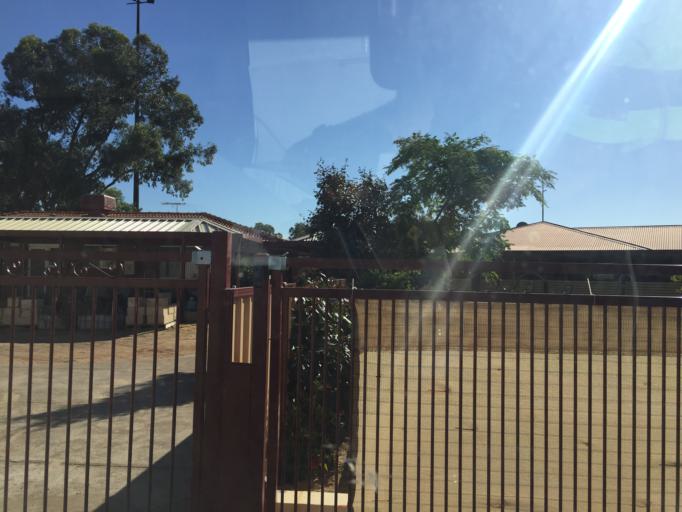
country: AU
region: Western Australia
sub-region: Mundaring
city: Swan View
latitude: -31.8840
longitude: 116.0395
